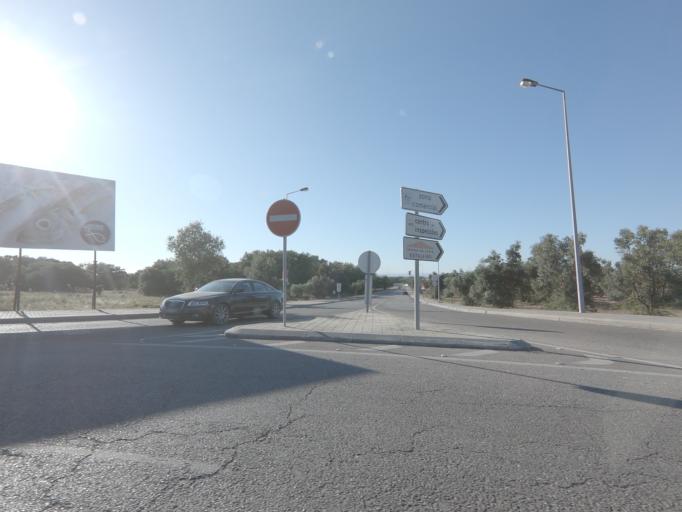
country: PT
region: Setubal
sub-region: Palmela
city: Quinta do Anjo
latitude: 38.5246
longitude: -8.9998
